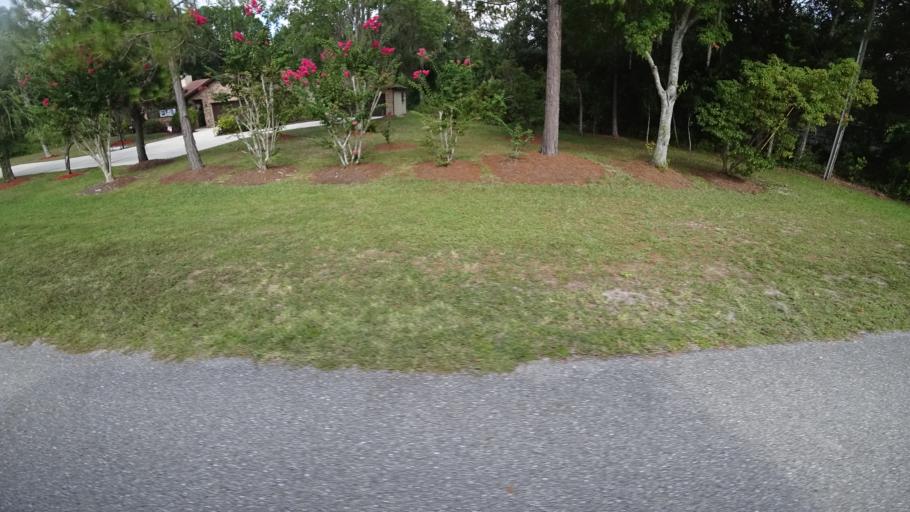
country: US
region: Florida
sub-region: Sarasota County
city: The Meadows
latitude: 27.4274
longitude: -82.4444
